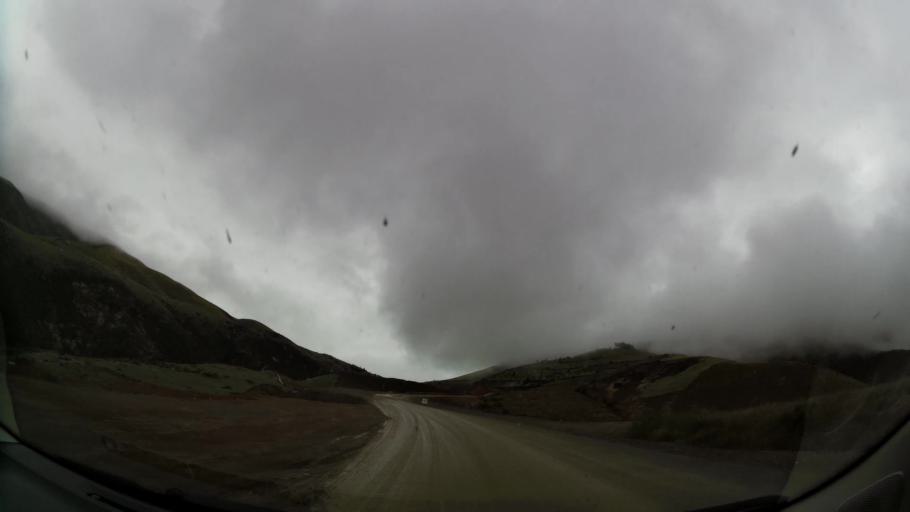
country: MA
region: Taza-Al Hoceima-Taounate
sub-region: Taza
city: Ajdir
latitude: 34.9119
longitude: -3.7968
